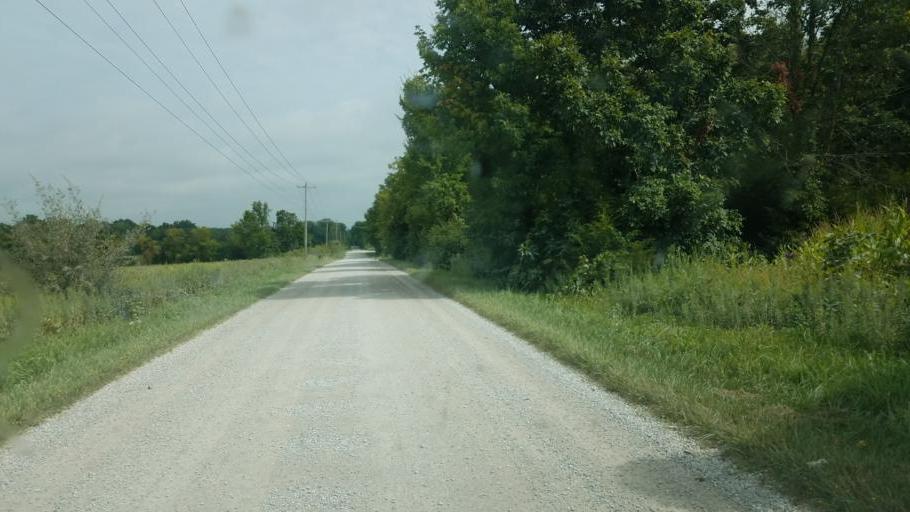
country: US
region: Ohio
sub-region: Morrow County
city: Cardington
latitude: 40.4065
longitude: -82.8521
